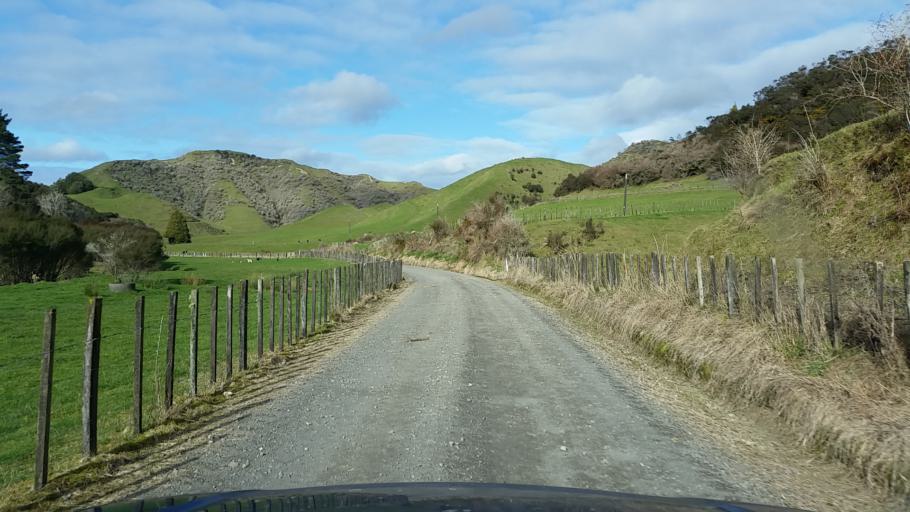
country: NZ
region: Taranaki
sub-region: South Taranaki District
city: Eltham
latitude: -39.2600
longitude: 174.5772
